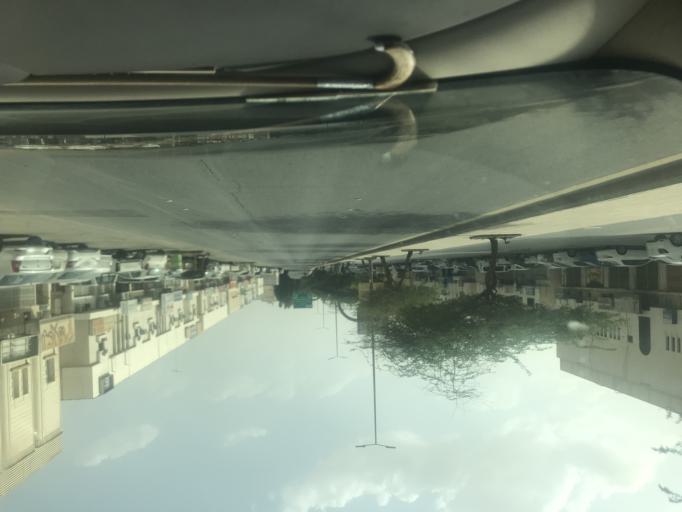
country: SA
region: Ar Riyad
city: Riyadh
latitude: 24.7283
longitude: 46.7643
